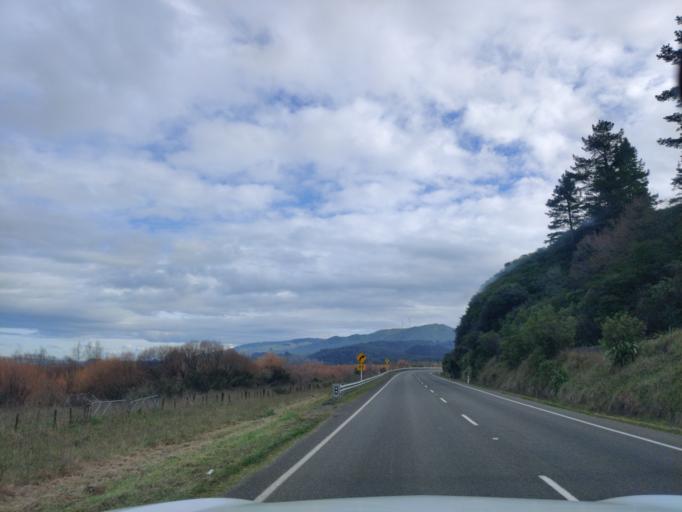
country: NZ
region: Manawatu-Wanganui
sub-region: Palmerston North City
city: Palmerston North
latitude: -40.3381
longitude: 175.8287
